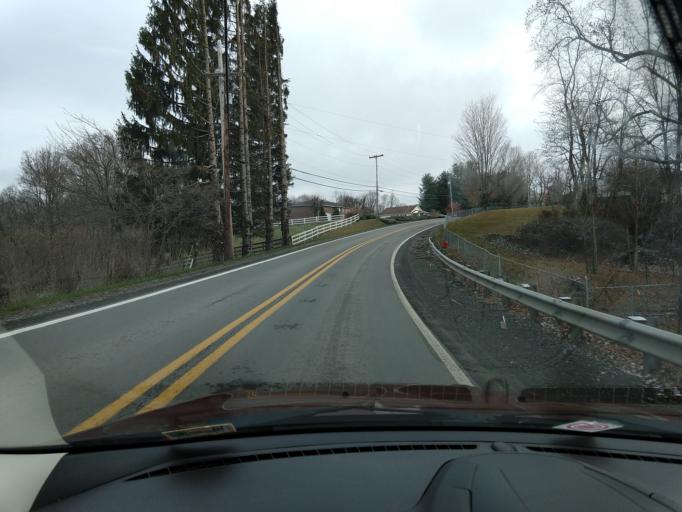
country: US
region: West Virginia
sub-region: Nicholas County
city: Craigsville
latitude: 38.2074
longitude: -80.6823
